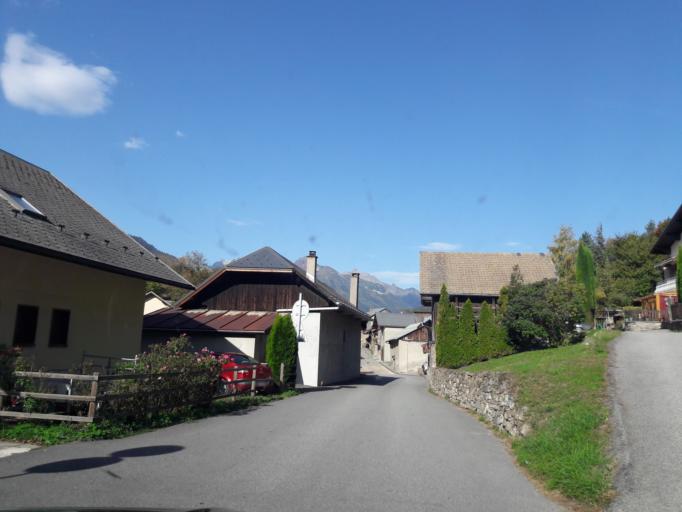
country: FR
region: Rhone-Alpes
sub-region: Departement de la Savoie
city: Saint-Jean-de-Maurienne
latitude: 45.3074
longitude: 6.3584
